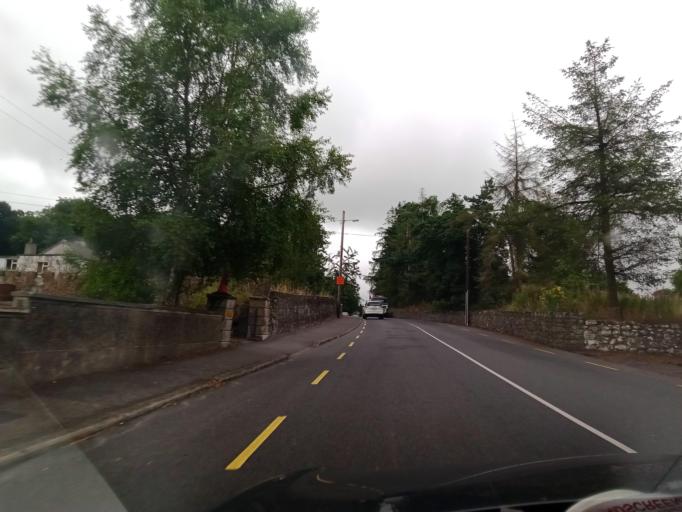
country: IE
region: Leinster
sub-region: Laois
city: Abbeyleix
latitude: 52.9119
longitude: -7.3401
